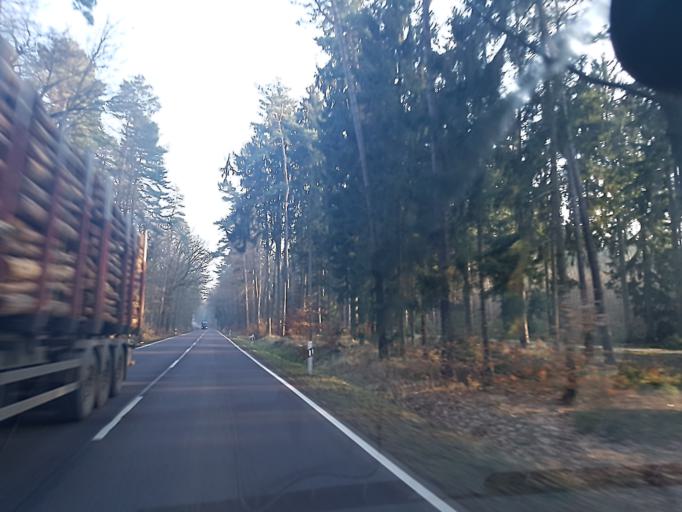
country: DE
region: Brandenburg
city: Wiesenburg
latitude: 52.1301
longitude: 12.4172
